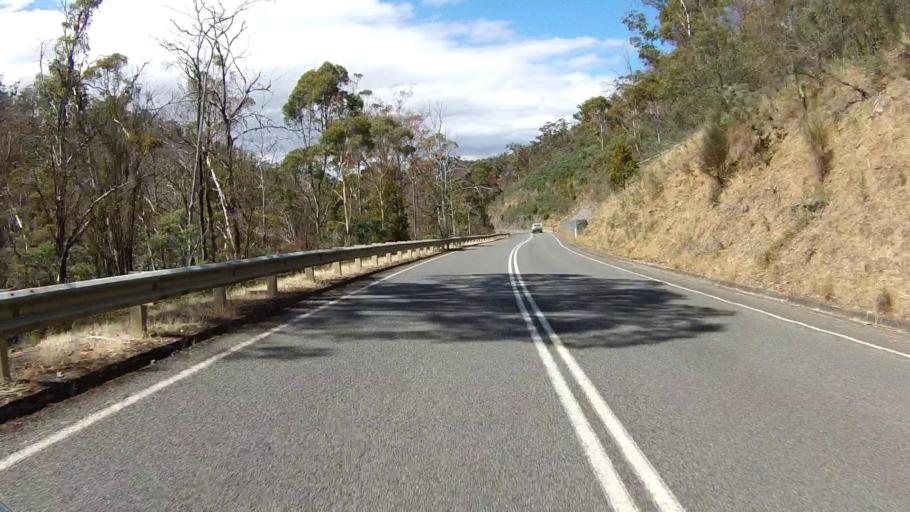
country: AU
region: Tasmania
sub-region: Sorell
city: Sorell
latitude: -42.6066
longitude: 147.6539
